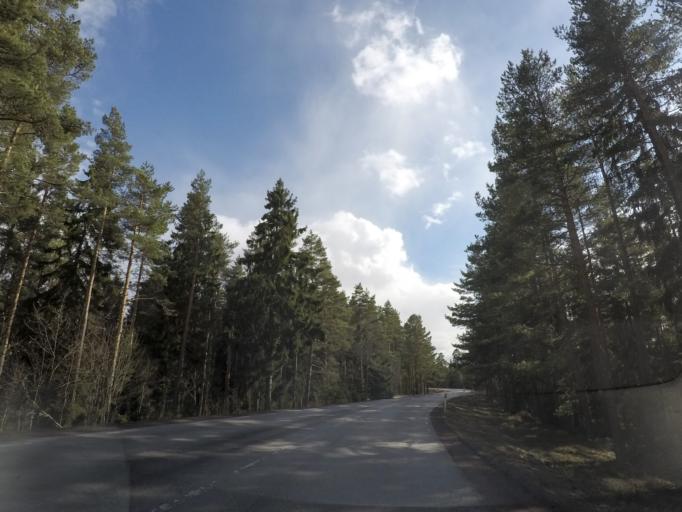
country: SE
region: Vaestmanland
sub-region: Hallstahammars Kommun
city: Hallstahammar
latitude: 59.6530
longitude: 16.1884
